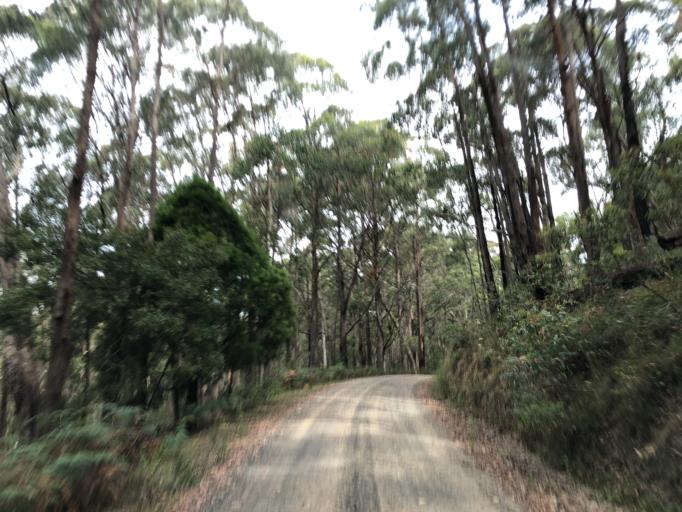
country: AU
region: Victoria
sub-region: Moorabool
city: Bacchus Marsh
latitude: -37.4651
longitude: 144.2783
